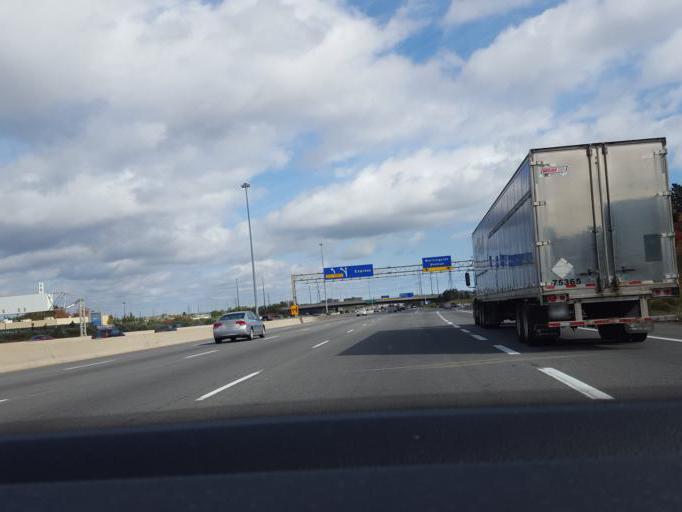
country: CA
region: Ontario
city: Scarborough
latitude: 43.7951
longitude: -79.2044
